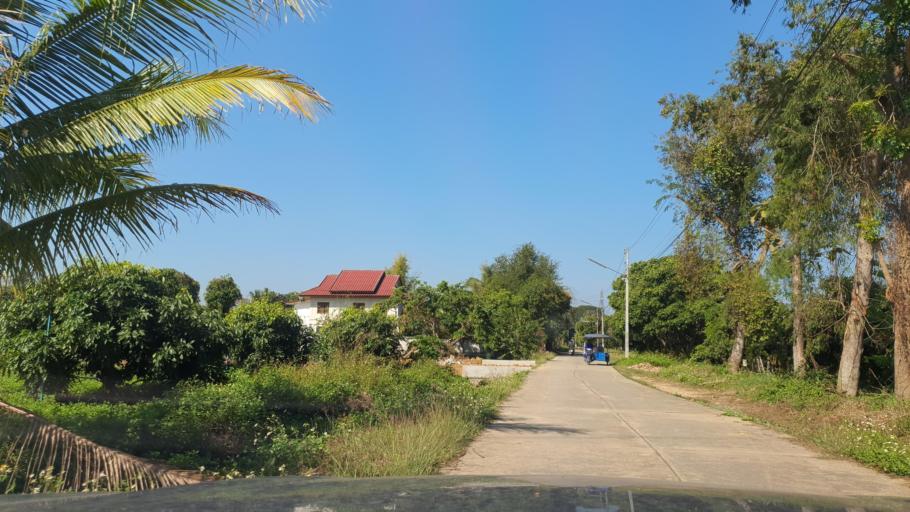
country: TH
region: Chiang Mai
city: Saraphi
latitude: 18.7028
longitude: 99.0724
